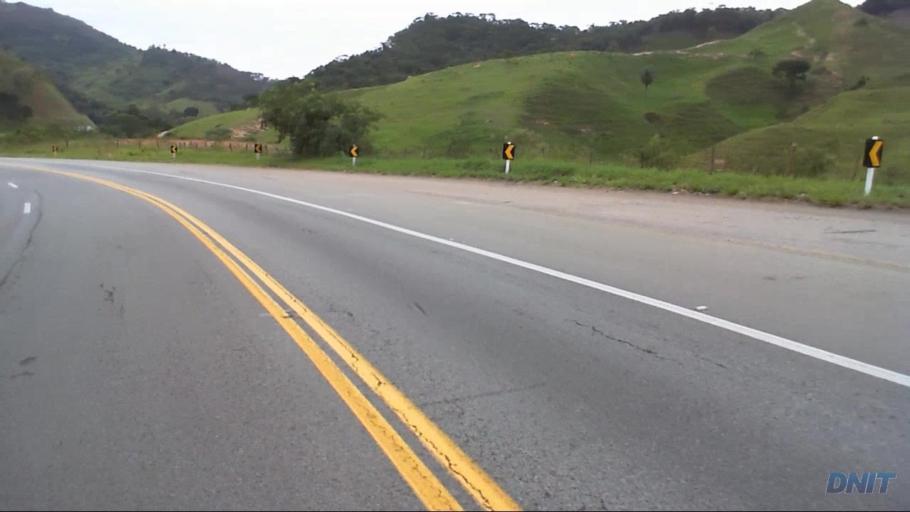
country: BR
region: Minas Gerais
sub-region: Nova Era
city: Nova Era
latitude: -19.6306
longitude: -42.8740
